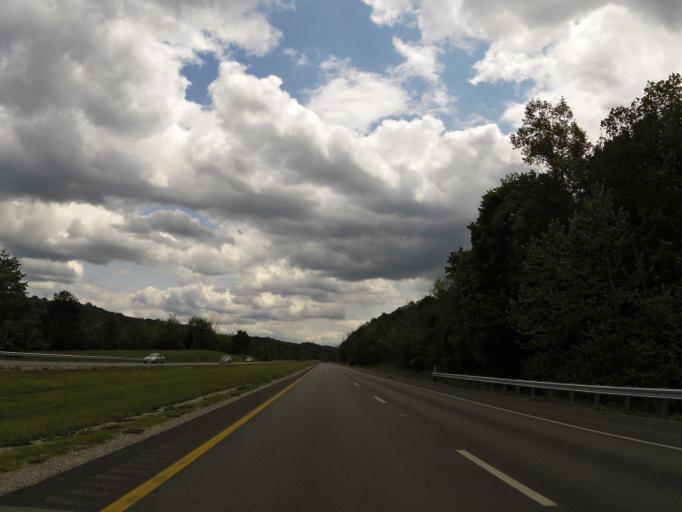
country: US
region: West Virginia
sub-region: Jackson County
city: Ripley
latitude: 38.7297
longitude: -81.6588
